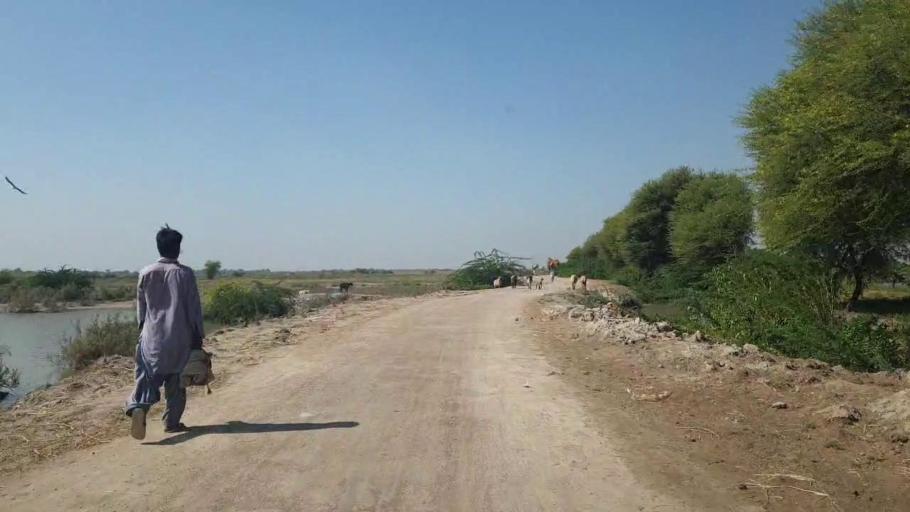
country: PK
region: Sindh
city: Talhar
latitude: 24.8030
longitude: 68.8132
